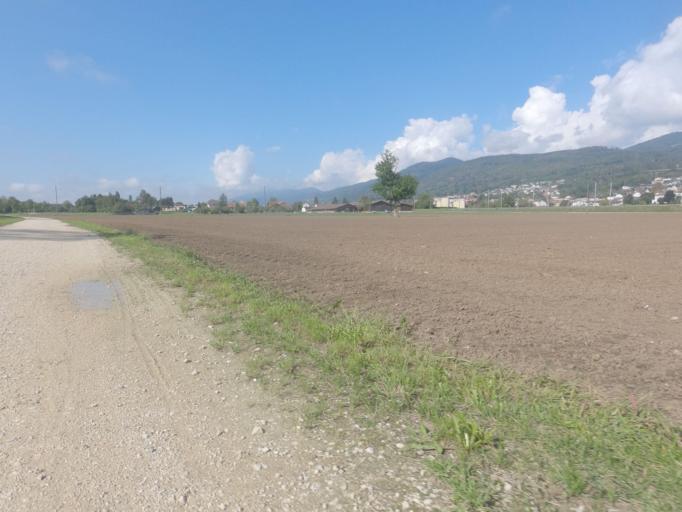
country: CH
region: Solothurn
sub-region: Bezirk Olten
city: Hagendorf
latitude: 47.3312
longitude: 7.8535
